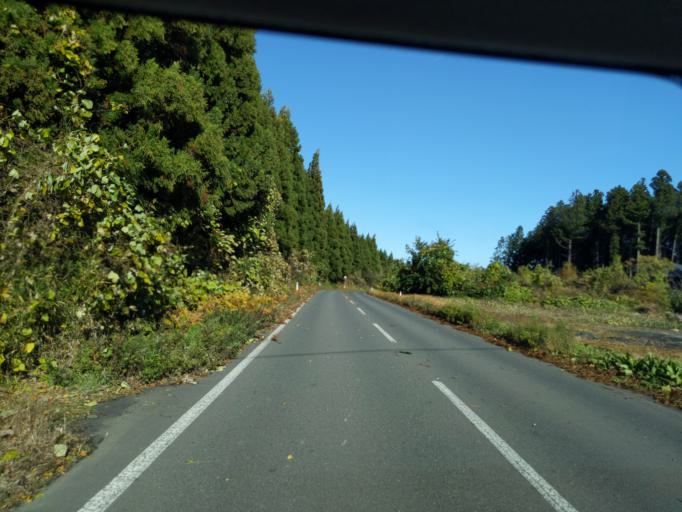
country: JP
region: Iwate
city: Mizusawa
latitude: 39.0912
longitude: 141.0958
